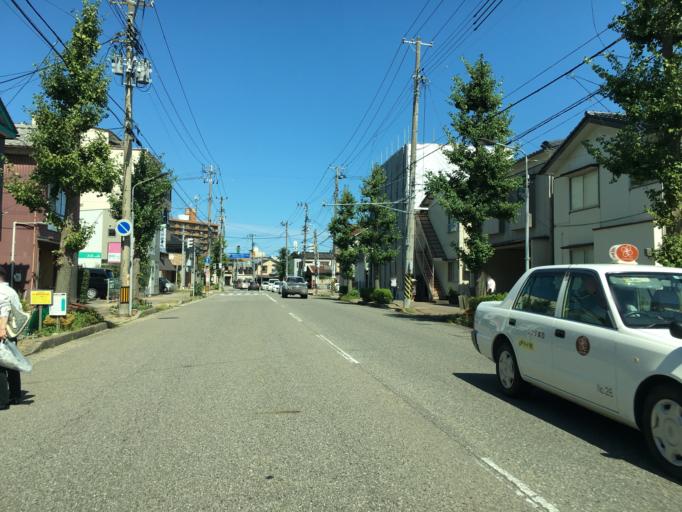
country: JP
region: Niigata
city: Niigata-shi
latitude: 37.9298
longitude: 139.0472
